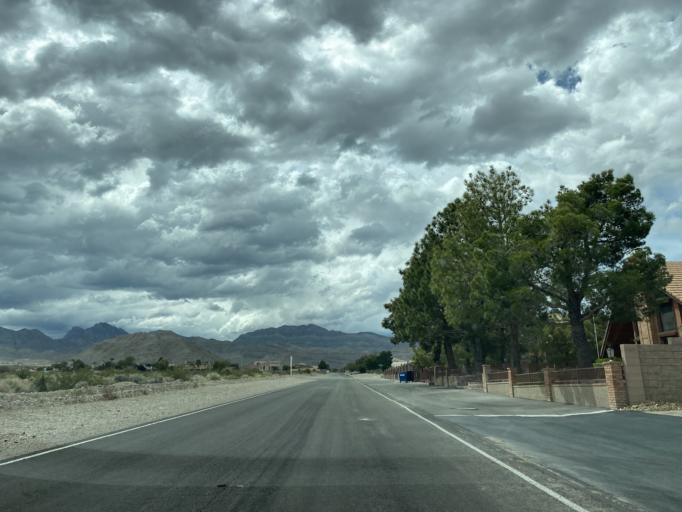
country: US
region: Nevada
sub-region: Clark County
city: Summerlin South
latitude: 36.2682
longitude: -115.3136
